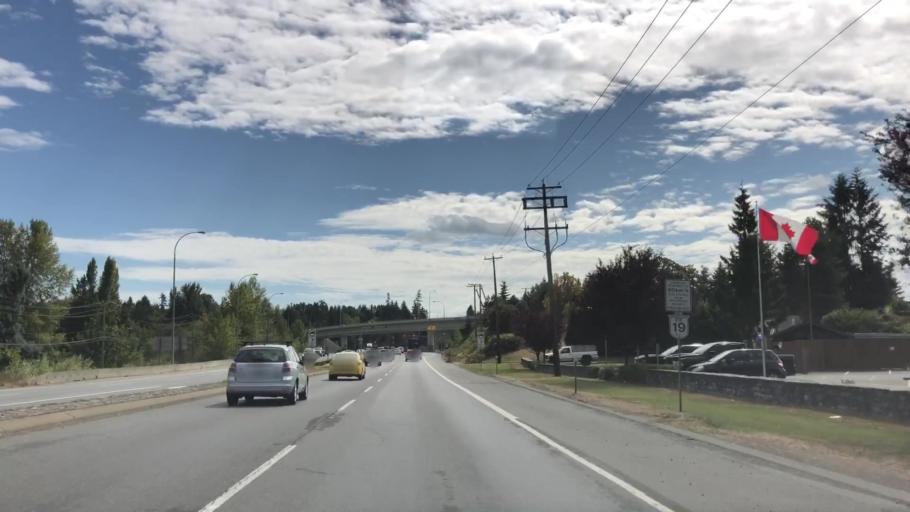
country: CA
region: British Columbia
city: Nanaimo
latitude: 49.1272
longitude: -123.9191
